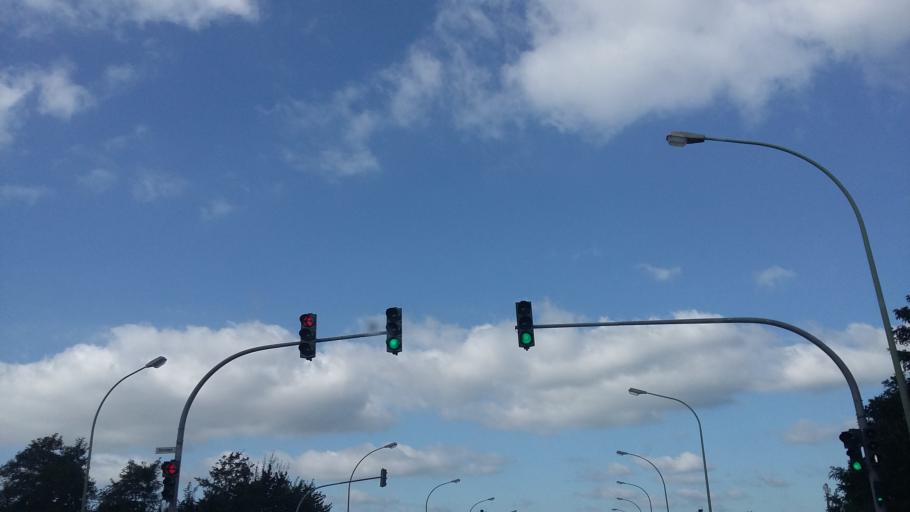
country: DE
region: Bremen
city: Bremerhaven
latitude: 53.5208
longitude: 8.5894
